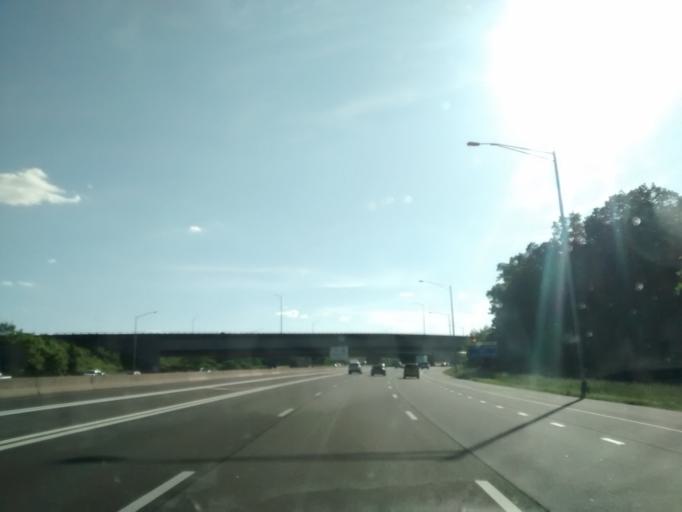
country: US
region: Connecticut
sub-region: Hartford County
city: East Hartford
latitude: 41.7739
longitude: -72.5800
